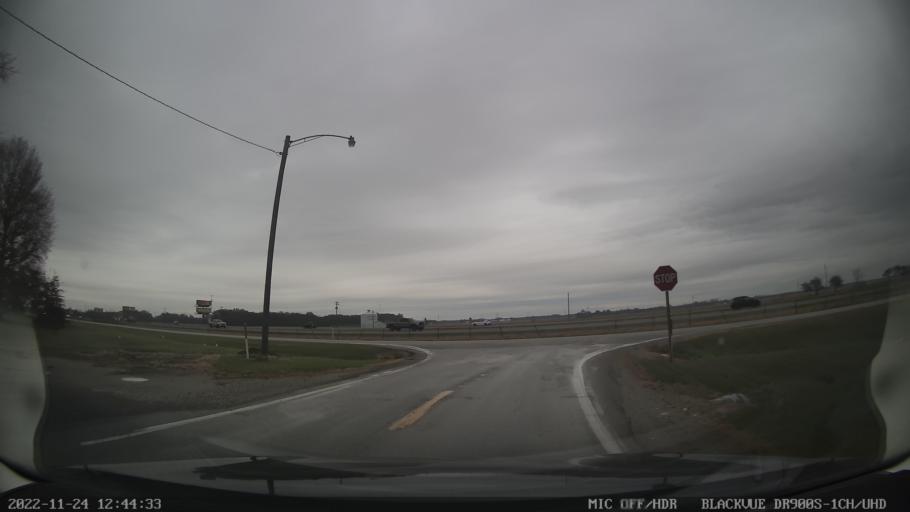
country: US
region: Illinois
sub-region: Macoupin County
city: Staunton
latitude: 38.9613
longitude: -89.7629
